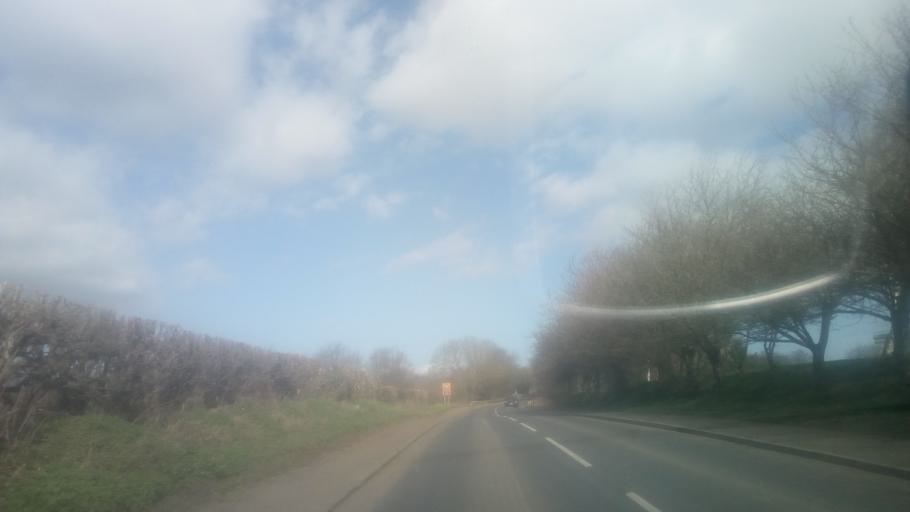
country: GB
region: Scotland
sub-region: East Lothian
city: Ormiston
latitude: 55.9149
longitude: -2.9355
